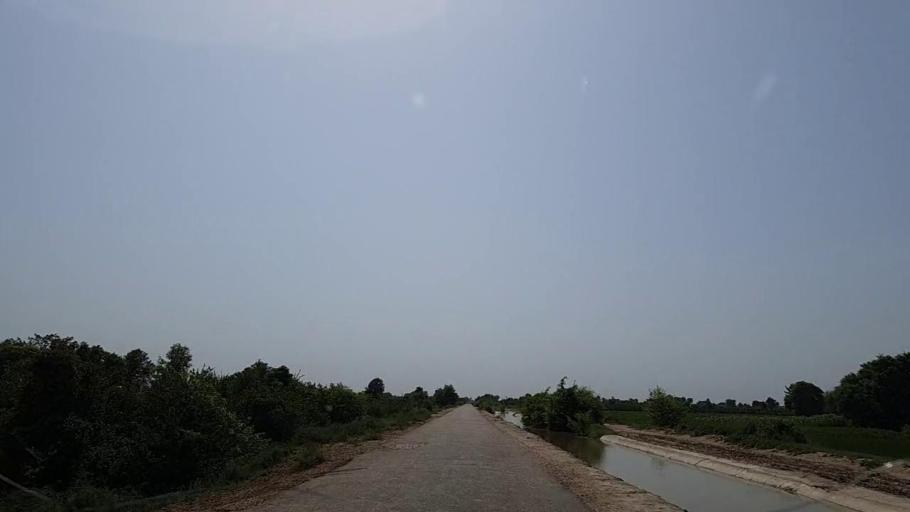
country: PK
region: Sindh
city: Kandiaro
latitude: 27.0504
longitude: 68.1604
